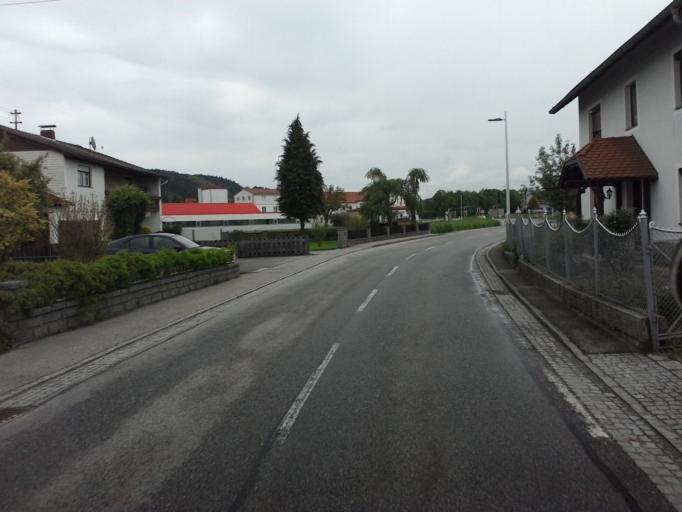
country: AT
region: Upper Austria
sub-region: Politischer Bezirk Scharding
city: Sankt Marienkirchen bei Schaerding
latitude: 48.3431
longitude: 13.4005
